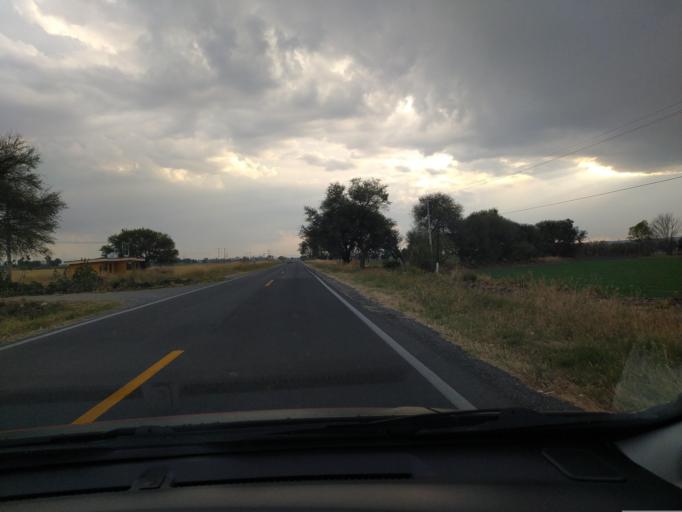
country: MX
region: Guanajuato
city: San Roque
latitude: 20.9592
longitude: -101.8678
